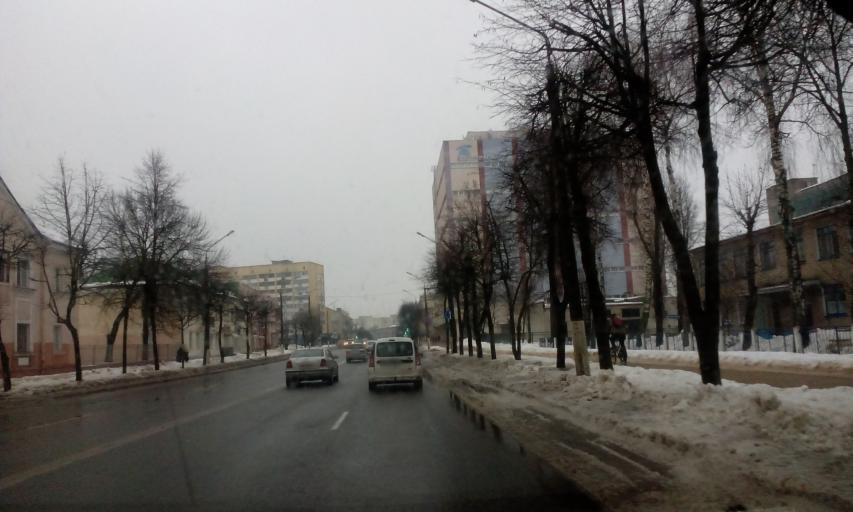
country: BY
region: Mogilev
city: Mahilyow
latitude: 53.8996
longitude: 30.3409
